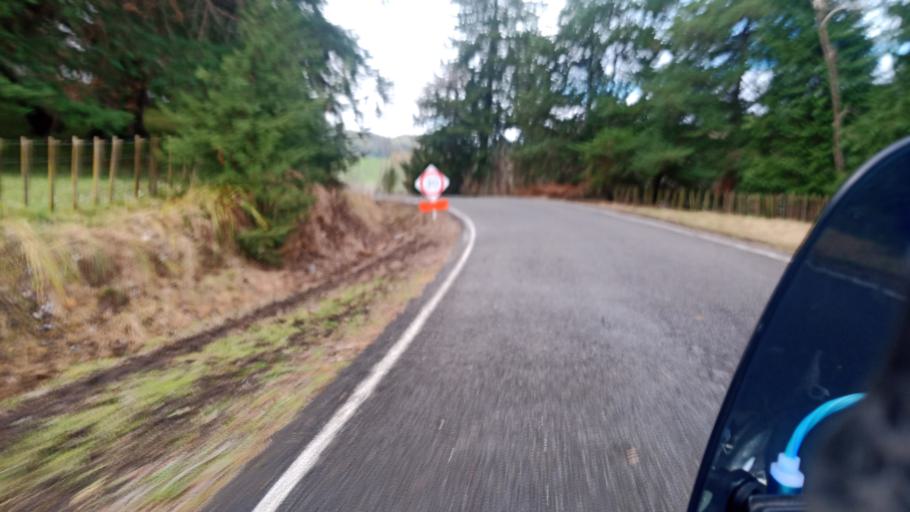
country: NZ
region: Gisborne
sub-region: Gisborne District
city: Gisborne
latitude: -38.4303
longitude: 177.9131
